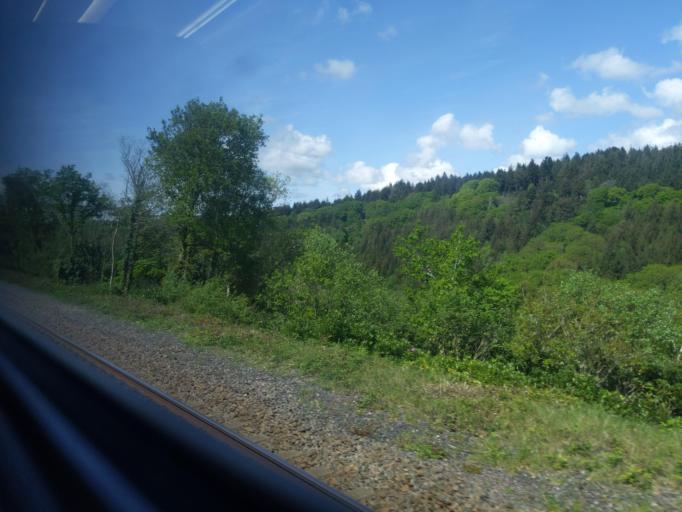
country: GB
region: England
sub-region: Cornwall
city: Lostwithiel
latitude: 50.4535
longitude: -4.5821
